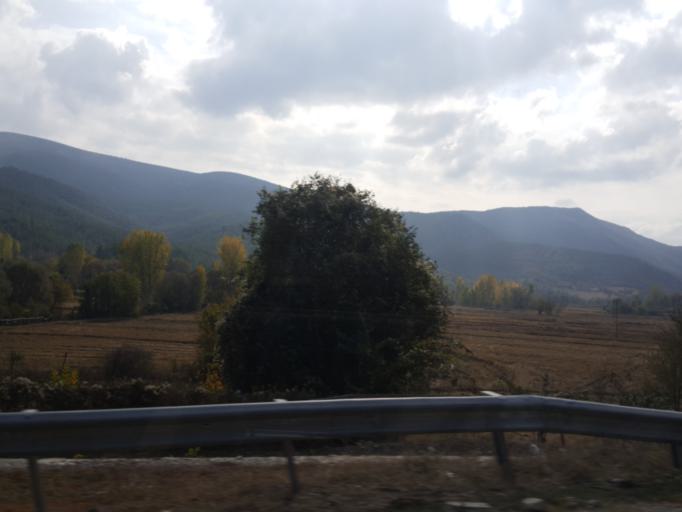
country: TR
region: Sinop
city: Sarayduzu
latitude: 41.3857
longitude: 34.9227
